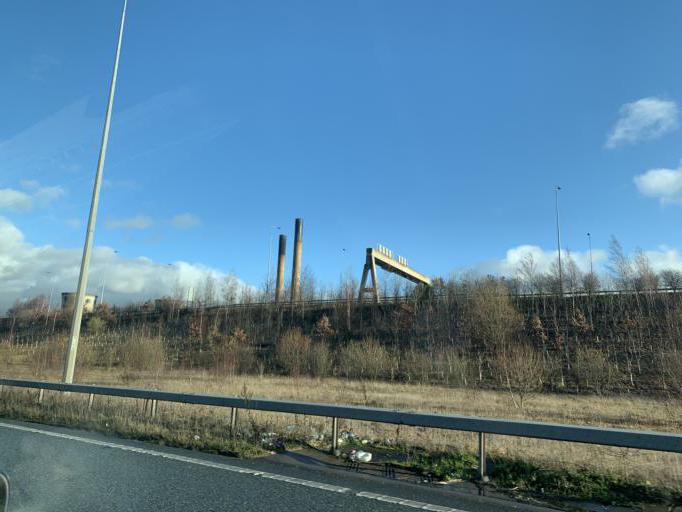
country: GB
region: England
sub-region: City and Borough of Wakefield
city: Ferrybridge
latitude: 53.7136
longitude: -1.2907
